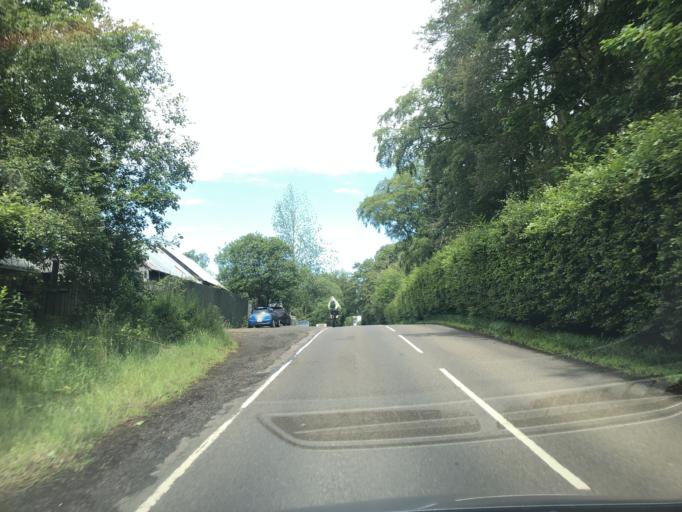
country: GB
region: Scotland
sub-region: Angus
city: Forfar
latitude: 56.6832
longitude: -2.9330
